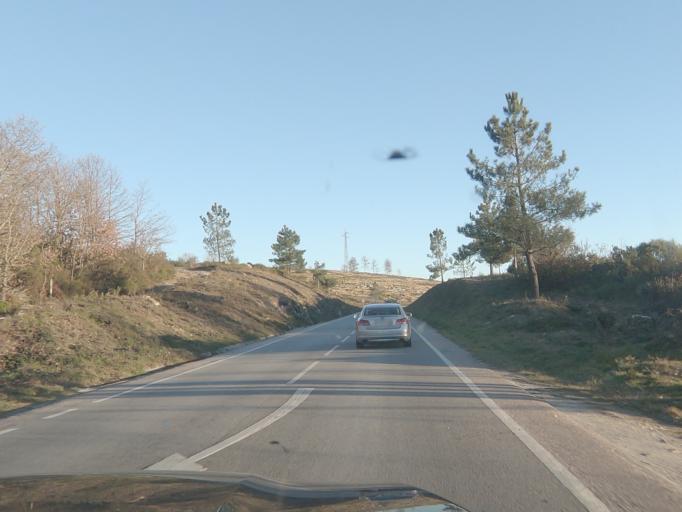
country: PT
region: Vila Real
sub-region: Ribeira de Pena
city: Ribeira de Pena
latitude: 41.5000
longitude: -7.7340
